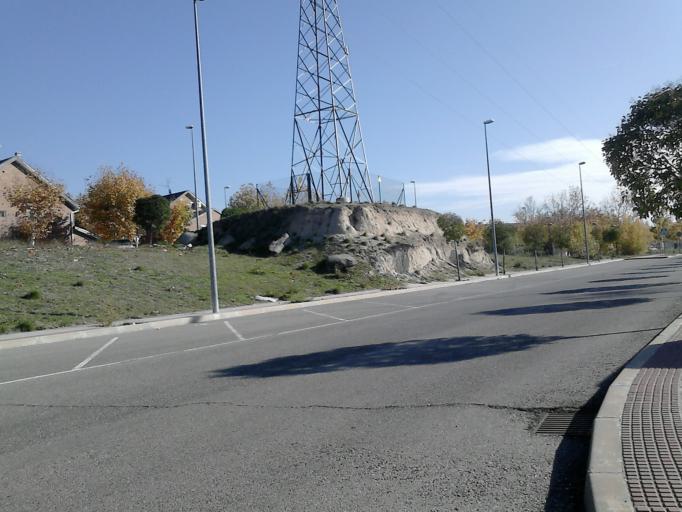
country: ES
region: Madrid
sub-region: Provincia de Madrid
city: Villanueva del Pardillo
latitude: 40.4992
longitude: -3.9705
